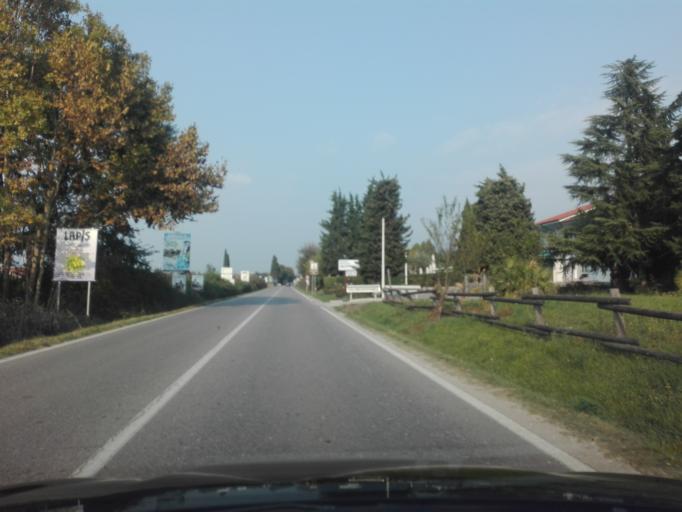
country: IT
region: Veneto
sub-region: Provincia di Verona
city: Cavalcaselle
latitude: 45.4484
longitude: 10.7114
